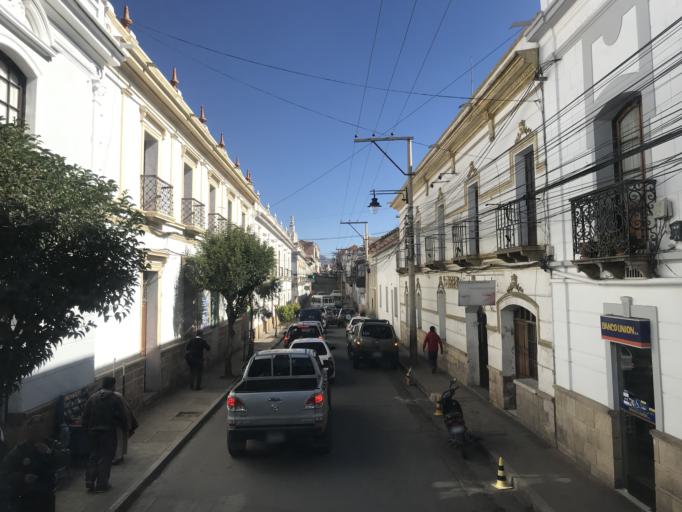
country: BO
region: Chuquisaca
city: Sucre
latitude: -19.0472
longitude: -65.2566
